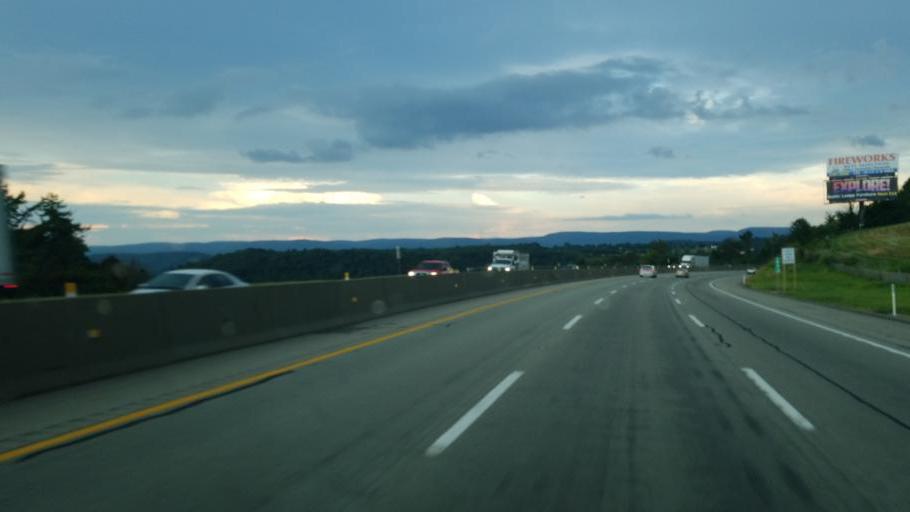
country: US
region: Pennsylvania
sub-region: Fayette County
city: Bear Rocks
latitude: 40.1237
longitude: -79.4010
